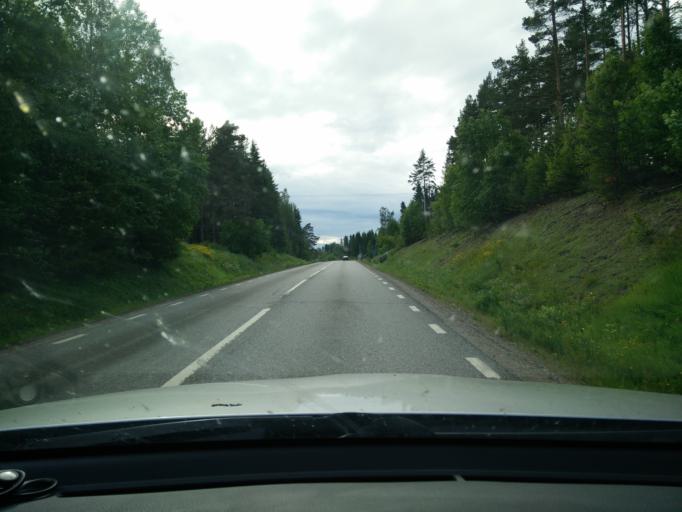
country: SE
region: Gaevleborg
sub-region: Nordanstigs Kommun
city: Bergsjoe
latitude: 62.0987
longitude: 16.7472
